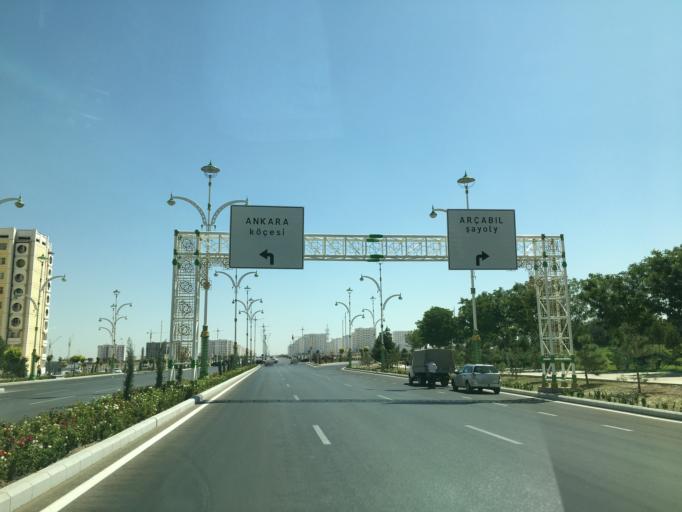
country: TM
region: Ahal
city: Ashgabat
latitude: 37.8954
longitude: 58.3948
